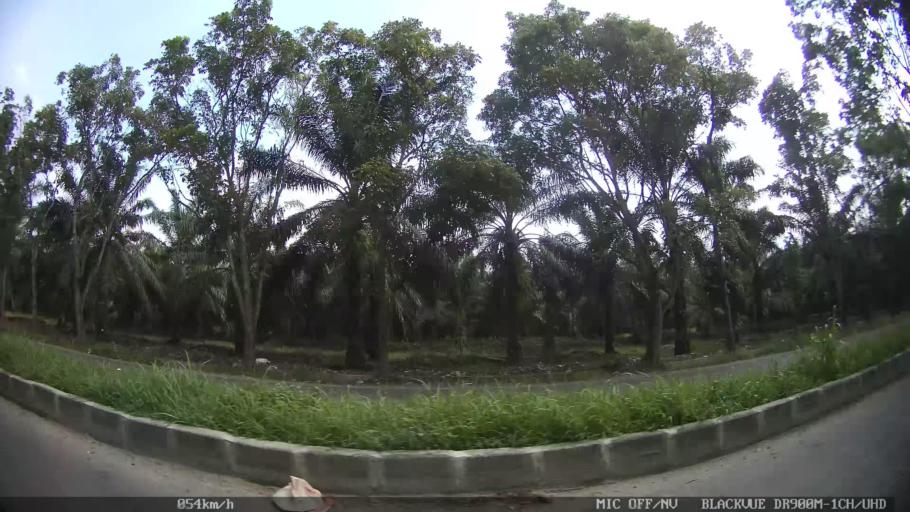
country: ID
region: North Sumatra
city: Binjai
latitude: 3.6512
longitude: 98.5304
